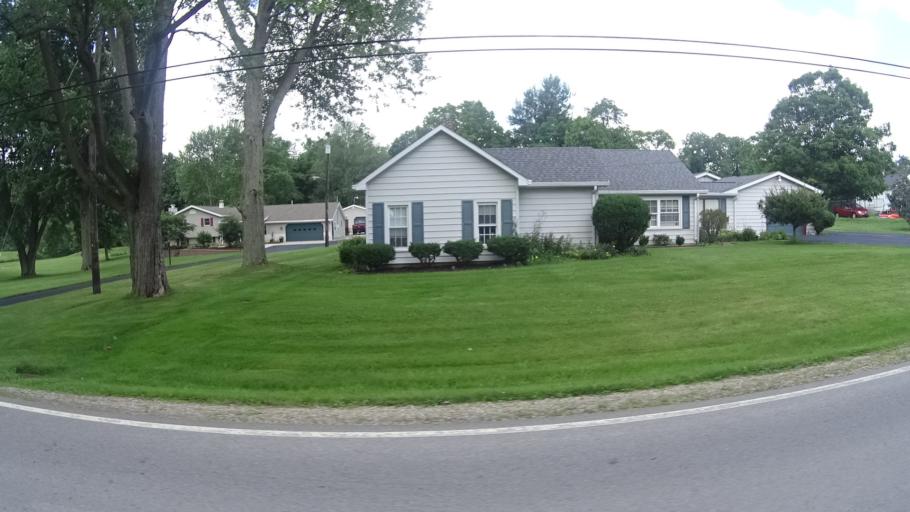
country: US
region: Ohio
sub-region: Huron County
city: Wakeman
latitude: 41.3190
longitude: -82.4137
